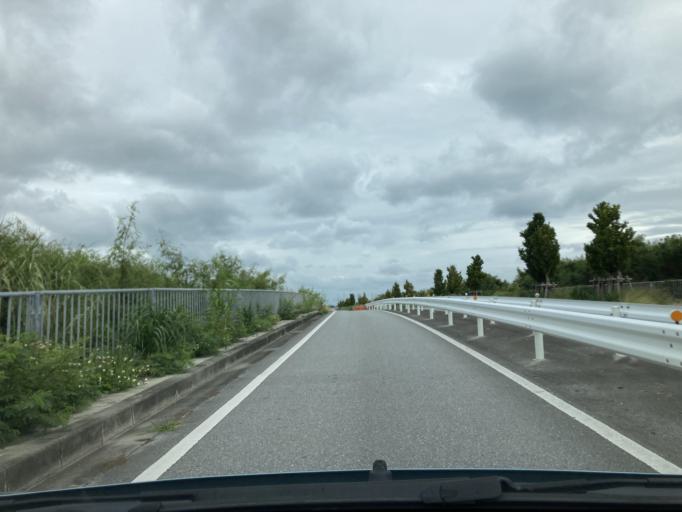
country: JP
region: Okinawa
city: Ginowan
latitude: 26.2115
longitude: 127.7659
